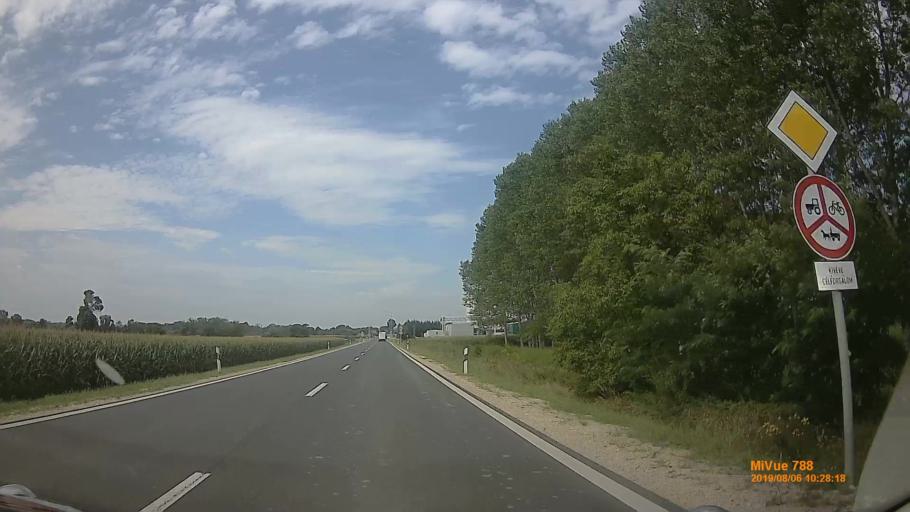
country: HU
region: Vas
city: Kormend
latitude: 47.0366
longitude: 16.6563
